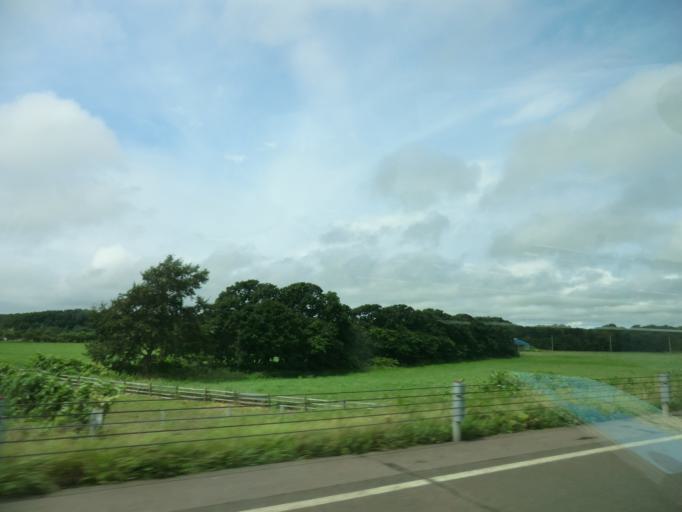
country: JP
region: Hokkaido
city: Kitahiroshima
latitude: 42.8730
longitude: 141.5537
